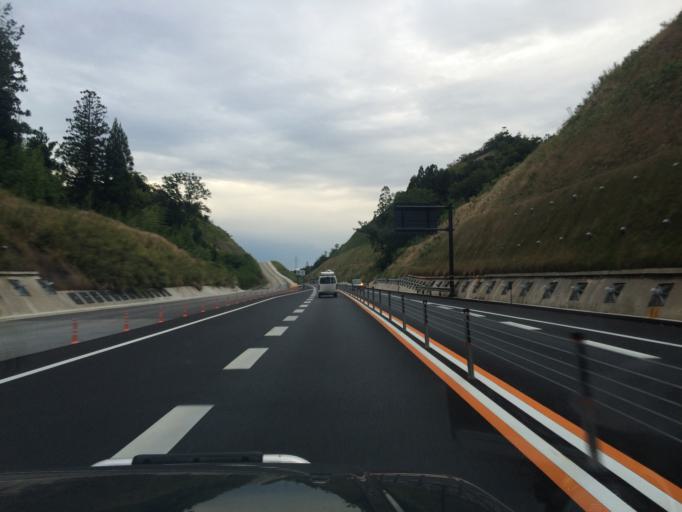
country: JP
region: Tottori
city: Tottori
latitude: 35.4928
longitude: 134.1387
